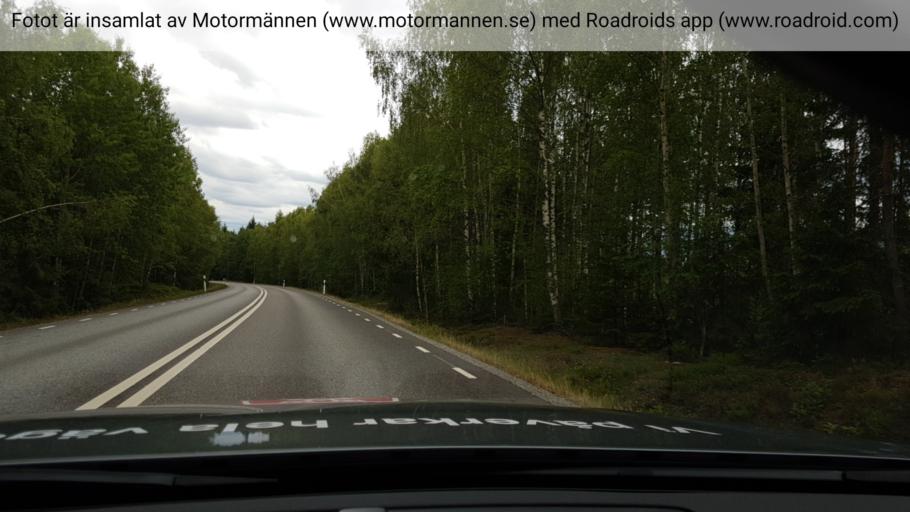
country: SE
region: Vaestmanland
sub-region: Skinnskattebergs Kommun
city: Skinnskatteberg
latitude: 59.8496
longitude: 15.6655
